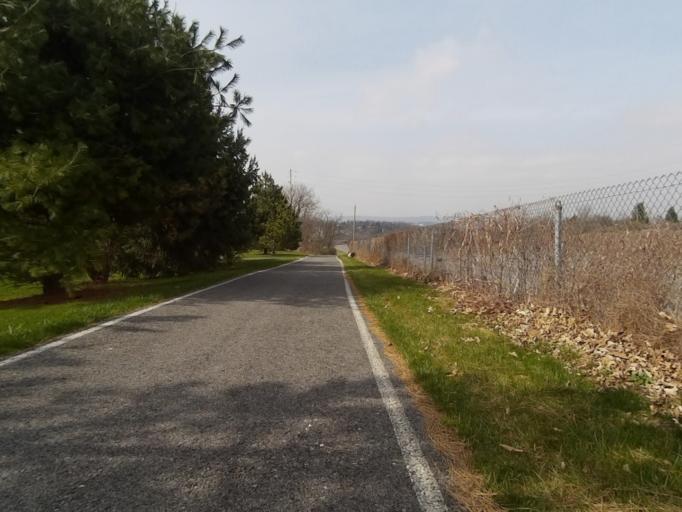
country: US
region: Pennsylvania
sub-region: Centre County
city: Lemont
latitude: 40.7969
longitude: -77.8228
